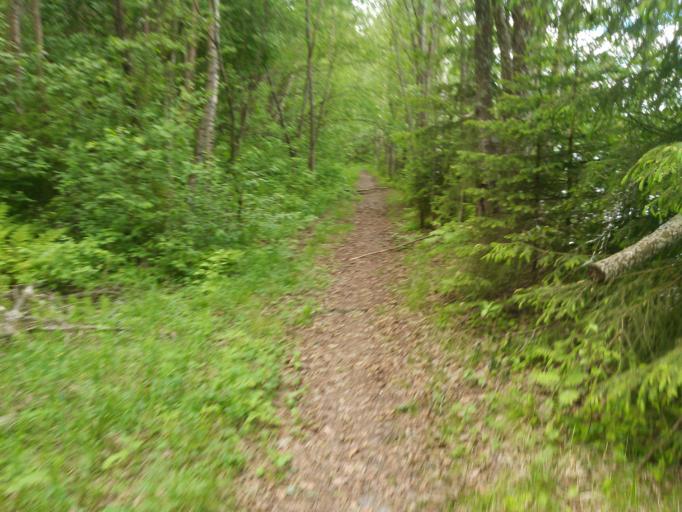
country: SE
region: Vaesterbotten
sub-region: Umea Kommun
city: Roback
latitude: 63.8236
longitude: 20.2018
